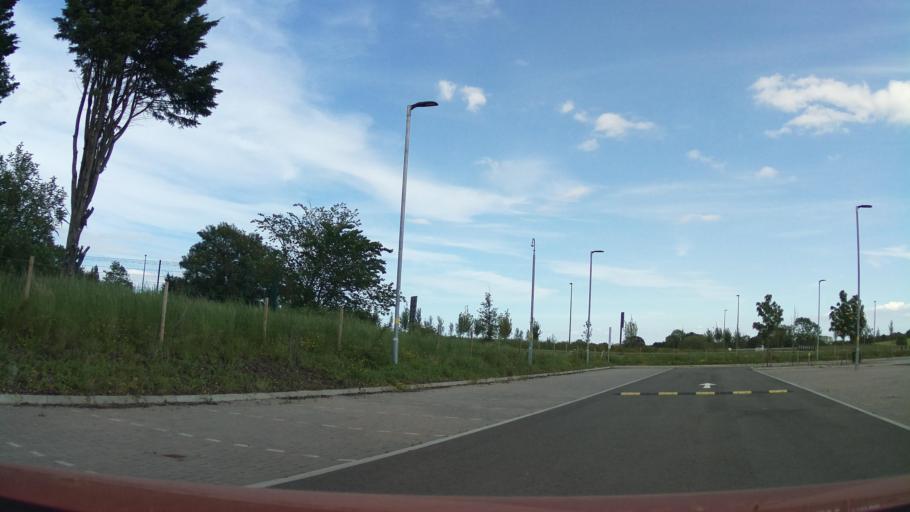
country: GB
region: England
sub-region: Worcestershire
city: Kempsey
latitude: 52.1580
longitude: -2.1584
